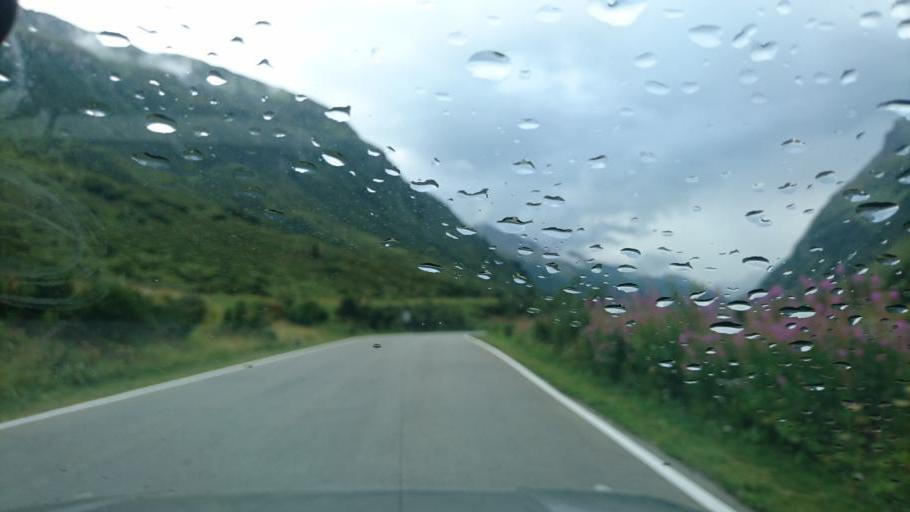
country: AT
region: Tyrol
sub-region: Politischer Bezirk Landeck
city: Galtur
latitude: 46.9543
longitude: 10.1525
